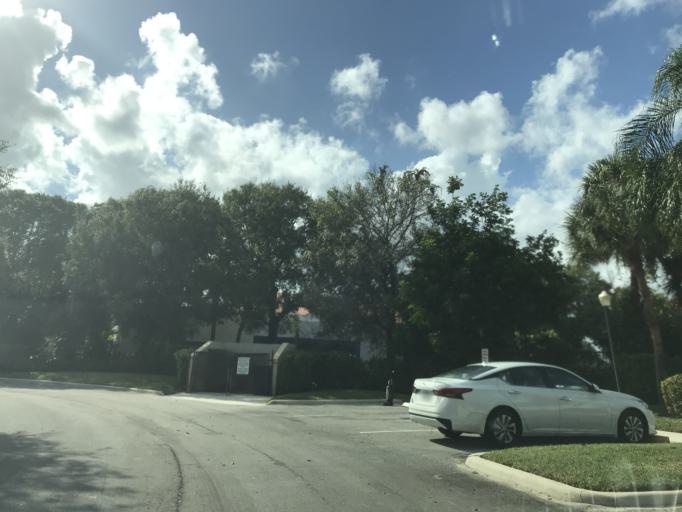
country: US
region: Florida
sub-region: Broward County
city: Coconut Creek
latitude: 26.2575
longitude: -80.1903
